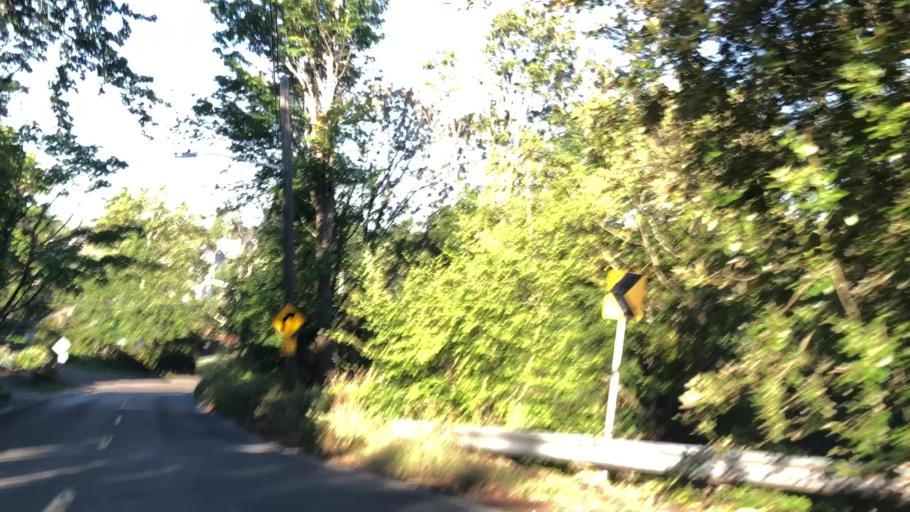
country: US
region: Washington
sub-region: King County
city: White Center
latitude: 47.5562
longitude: -122.3552
